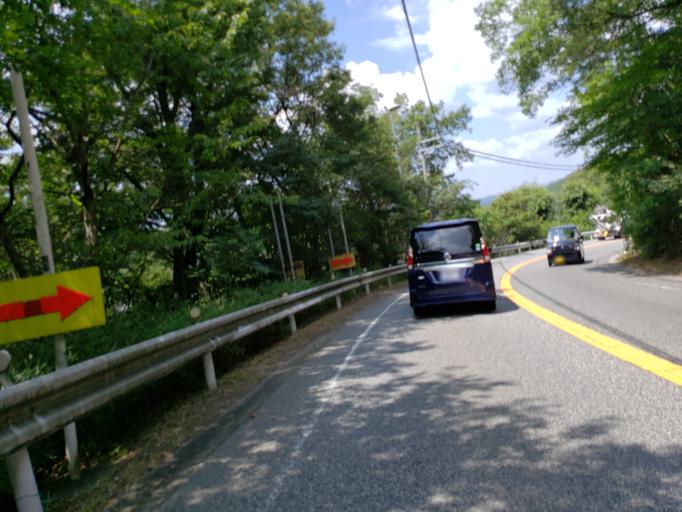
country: JP
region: Hyogo
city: Aioi
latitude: 34.7991
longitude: 134.4498
